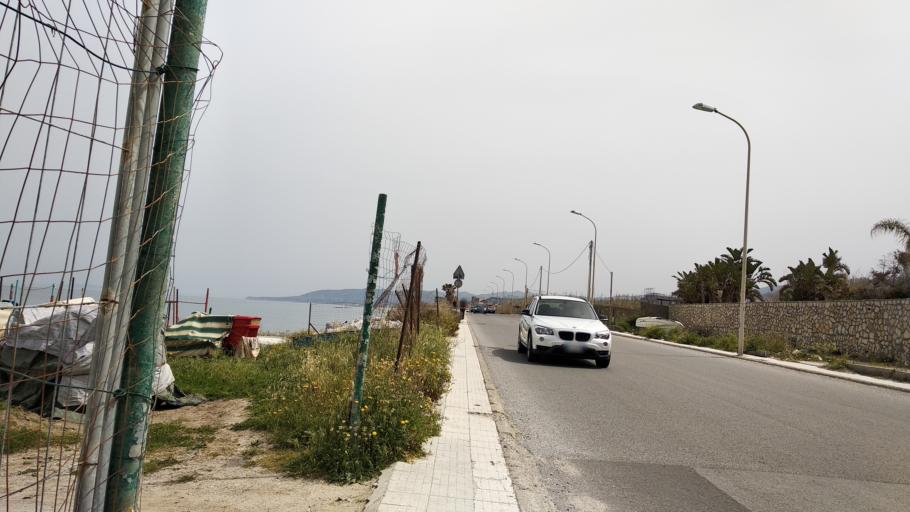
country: IT
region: Sicily
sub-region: Messina
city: Torregrotta
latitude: 38.2157
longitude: 15.3460
